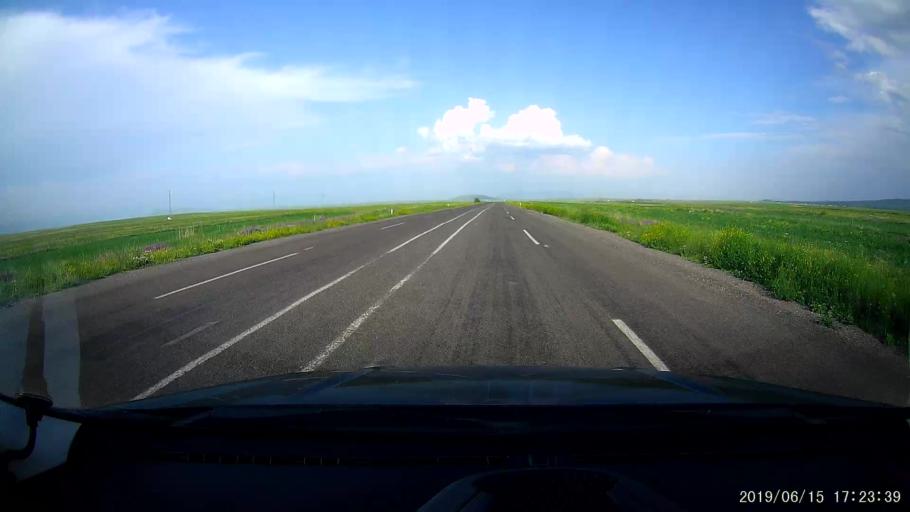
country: TR
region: Kars
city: Basgedikler
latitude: 40.6167
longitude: 43.3676
